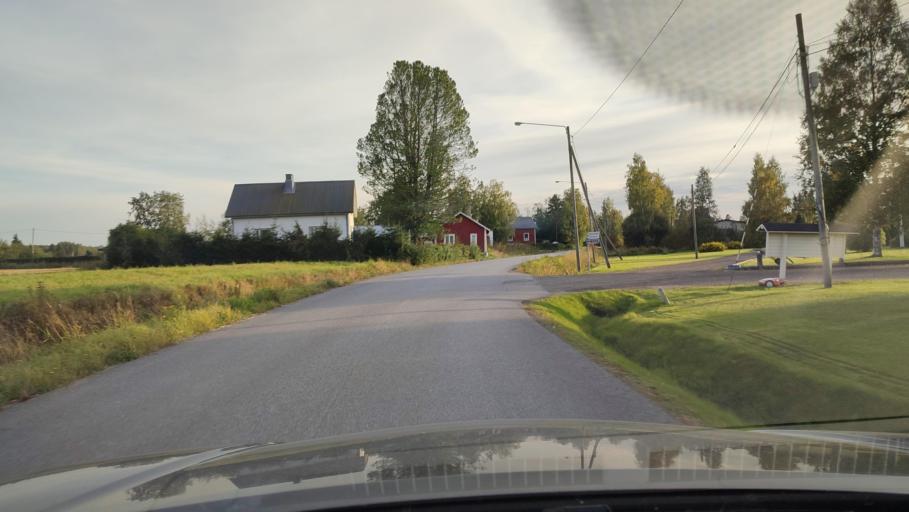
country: FI
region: Ostrobothnia
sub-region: Sydosterbotten
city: Kristinestad
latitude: 62.2531
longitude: 21.5087
